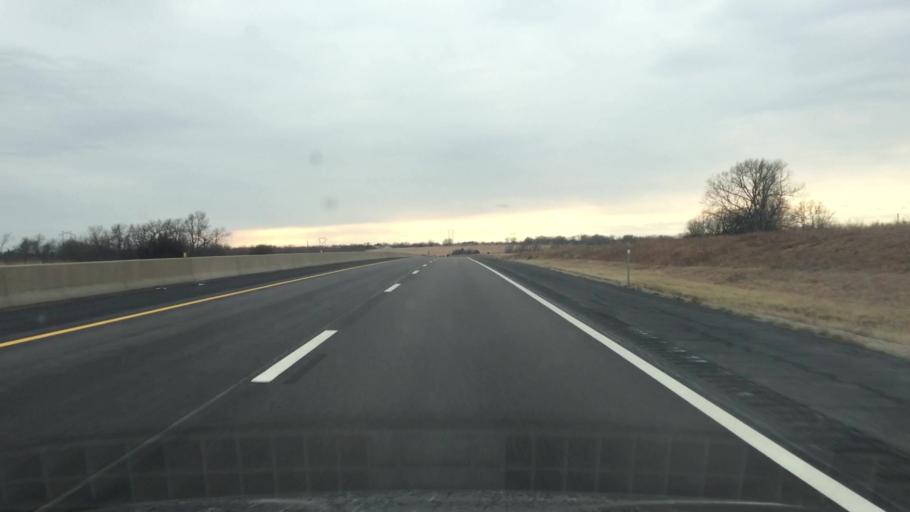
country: US
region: Kansas
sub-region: Shawnee County
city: Auburn
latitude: 38.8341
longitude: -95.8809
